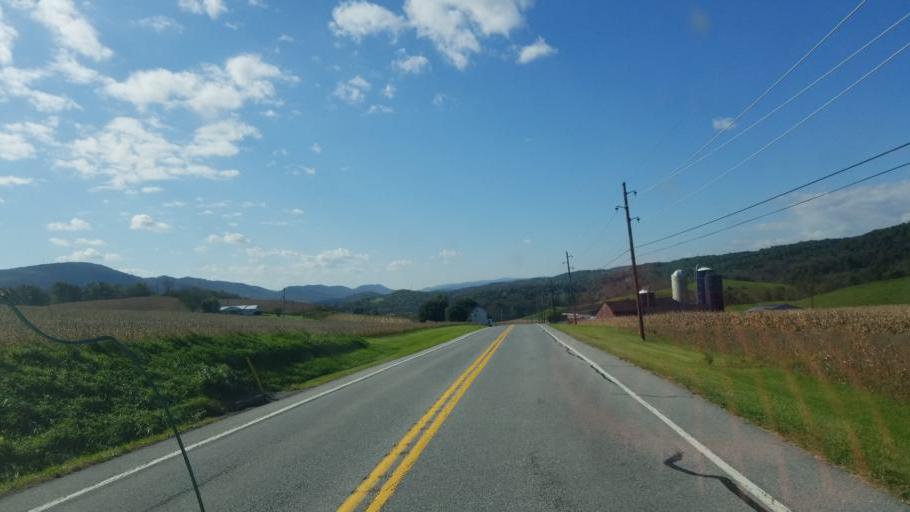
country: US
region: Pennsylvania
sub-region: Bedford County
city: Bedford
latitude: 40.0676
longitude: -78.5472
